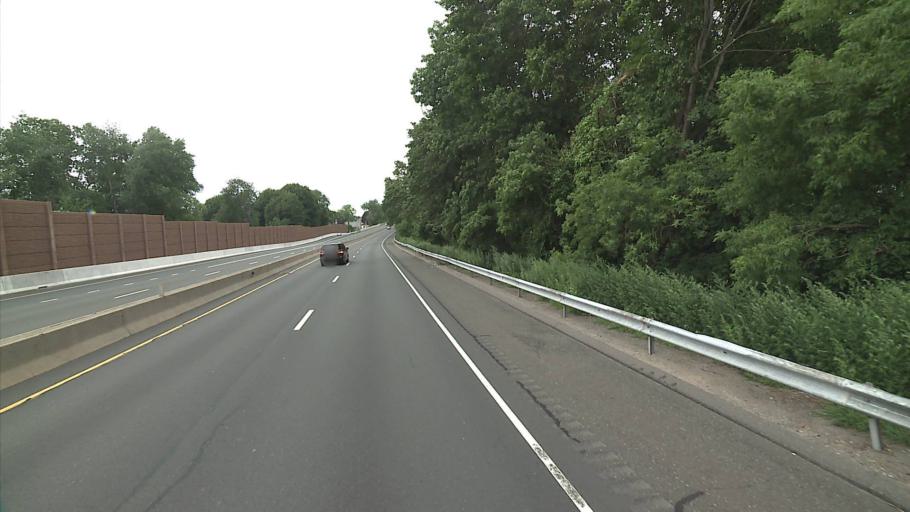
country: US
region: Connecticut
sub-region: New Haven County
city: Ansonia
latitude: 41.3442
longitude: -73.0932
